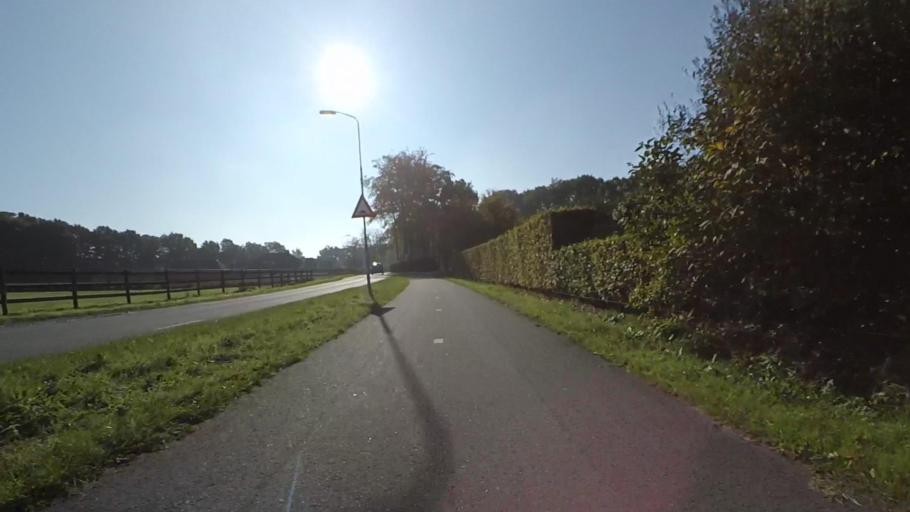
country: NL
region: Gelderland
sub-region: Gemeente Putten
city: Putten
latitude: 52.2713
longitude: 5.6030
